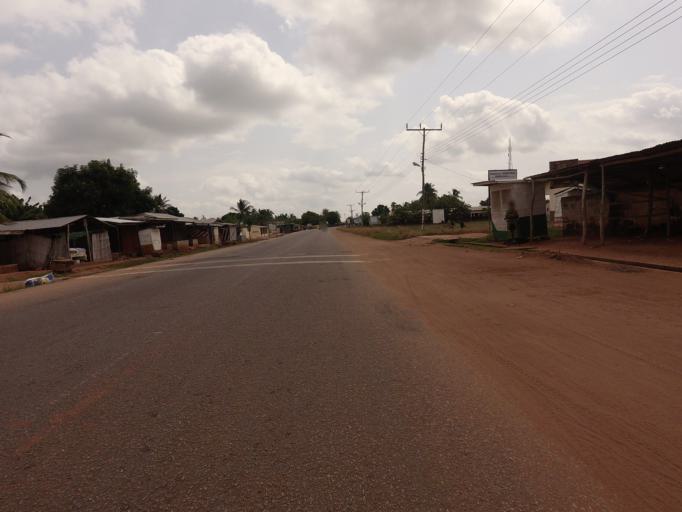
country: TG
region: Maritime
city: Lome
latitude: 6.2217
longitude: 1.0369
